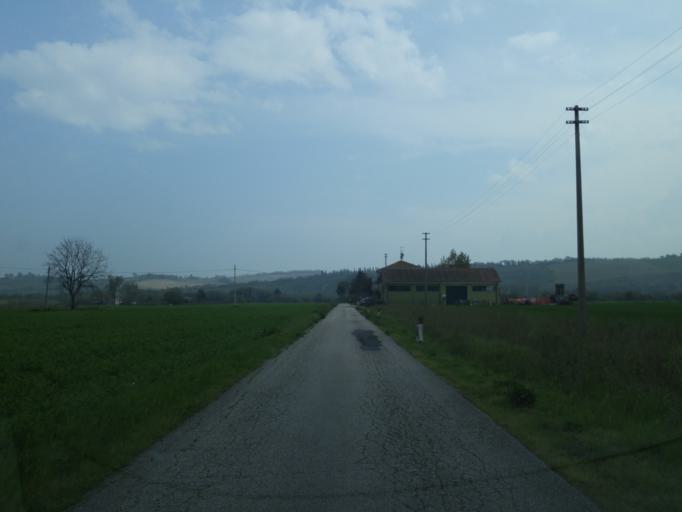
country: IT
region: The Marches
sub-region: Provincia di Pesaro e Urbino
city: Bellocchi
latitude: 43.7823
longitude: 12.9921
